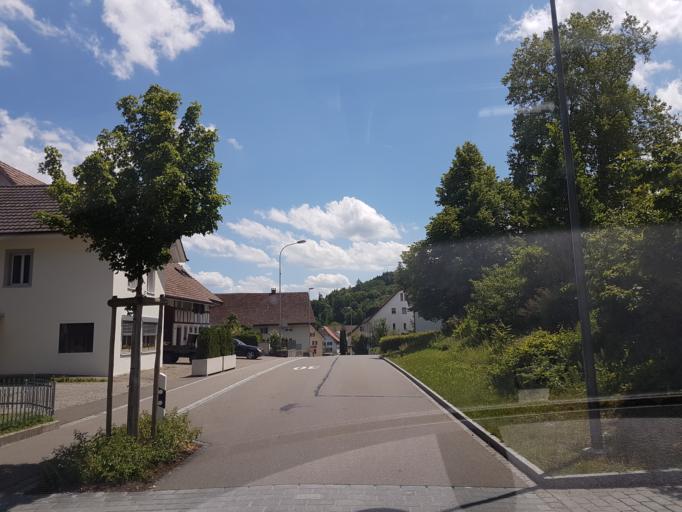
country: CH
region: Aargau
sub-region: Bezirk Baden
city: Mellingen
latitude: 47.4125
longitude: 8.2571
